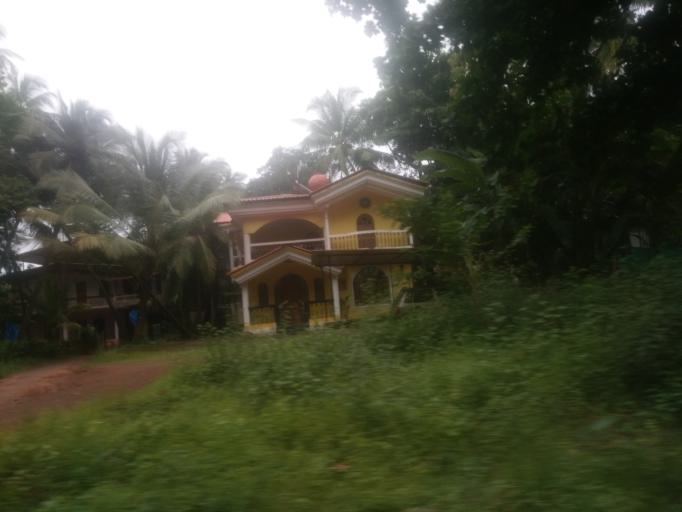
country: IN
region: Goa
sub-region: South Goa
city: Varca
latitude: 15.2162
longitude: 73.9500
